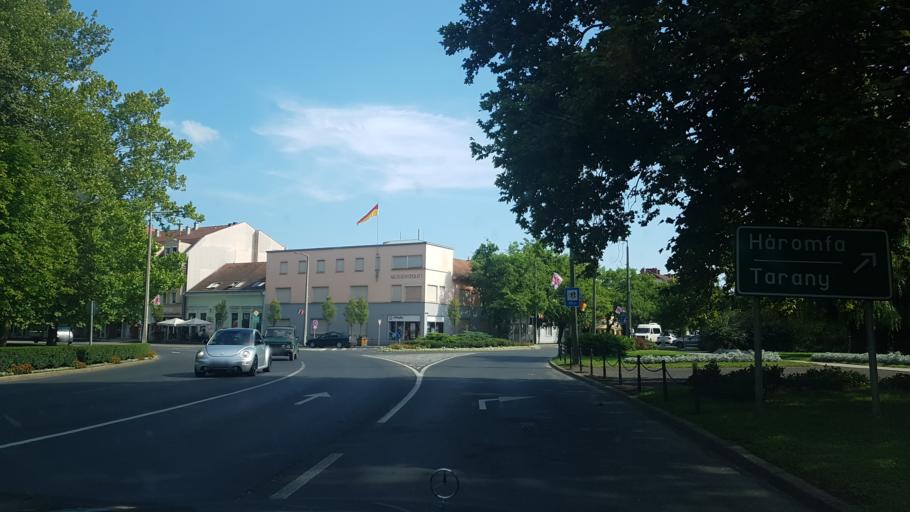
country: HU
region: Somogy
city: Nagyatad
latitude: 46.2286
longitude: 17.3630
